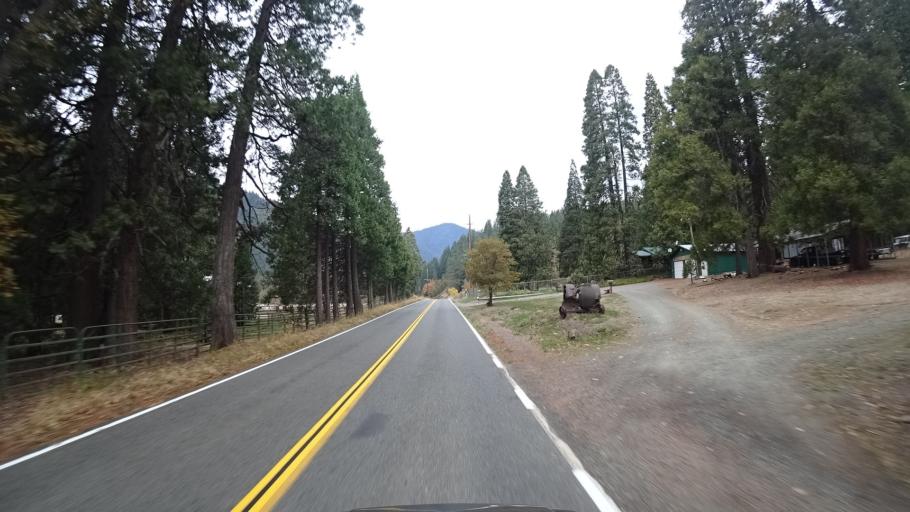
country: US
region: California
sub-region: Siskiyou County
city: Happy Camp
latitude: 41.8748
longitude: -123.4130
